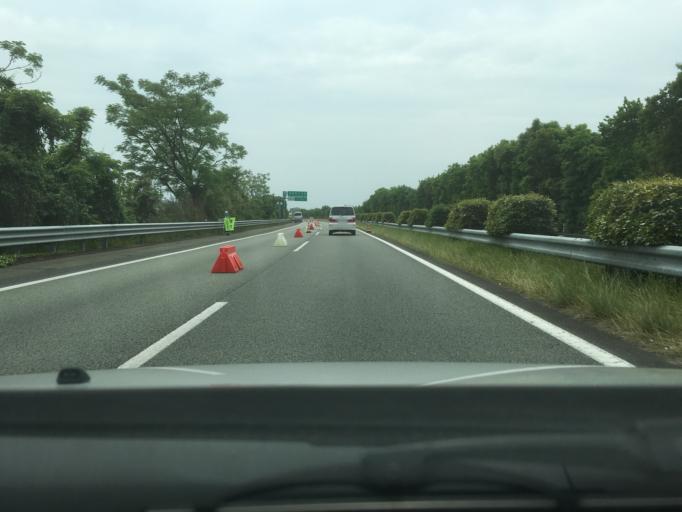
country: JP
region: Kumamoto
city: Kumamoto
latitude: 32.7991
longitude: 130.7908
